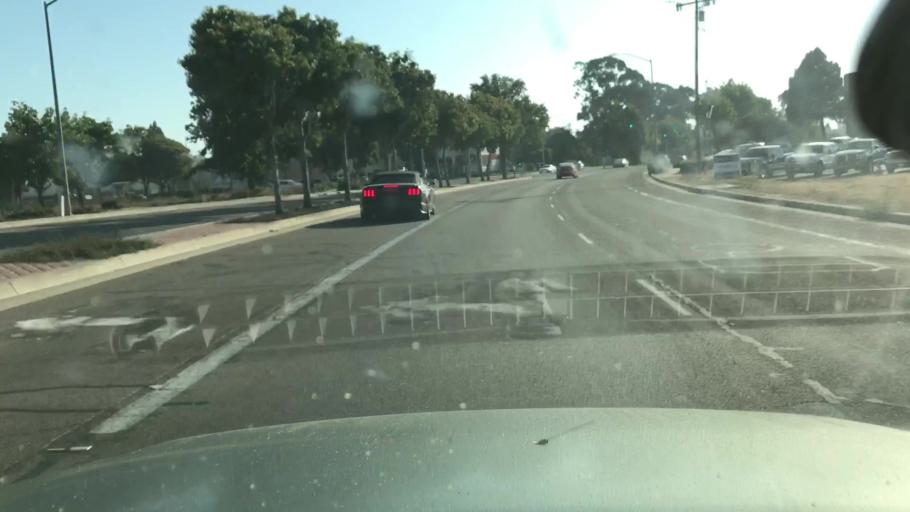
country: US
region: California
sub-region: Santa Barbara County
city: Santa Maria
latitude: 34.9103
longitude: -120.4330
